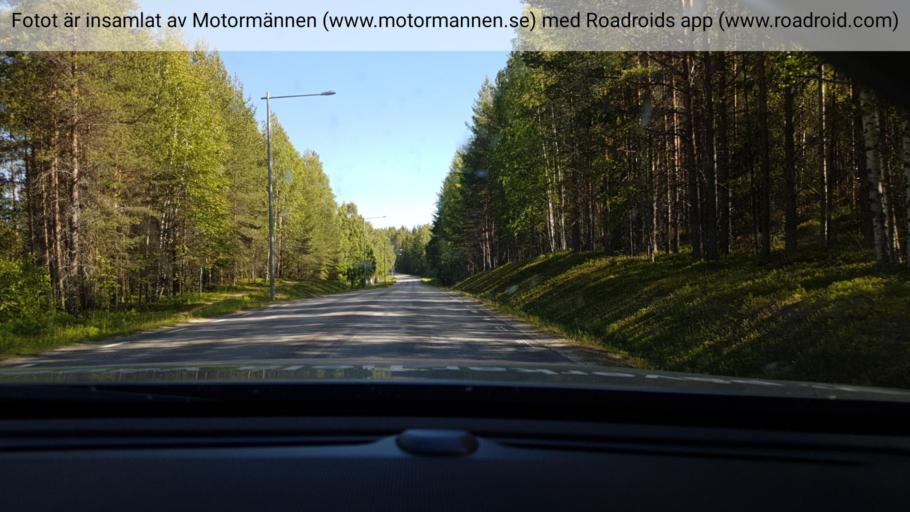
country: SE
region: Vaesterbotten
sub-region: Lycksele Kommun
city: Lycksele
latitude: 64.6119
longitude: 18.6440
